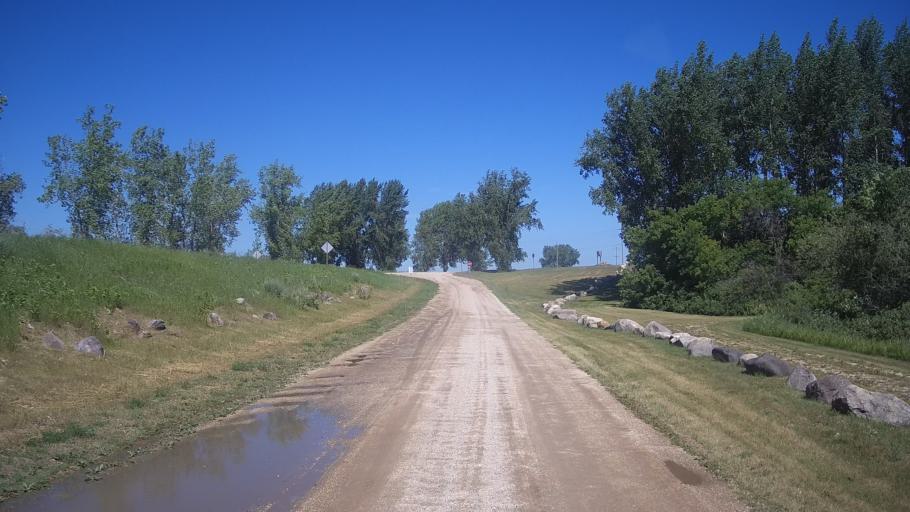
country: CA
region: Manitoba
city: Portage la Prairie
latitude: 49.9480
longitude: -98.3314
